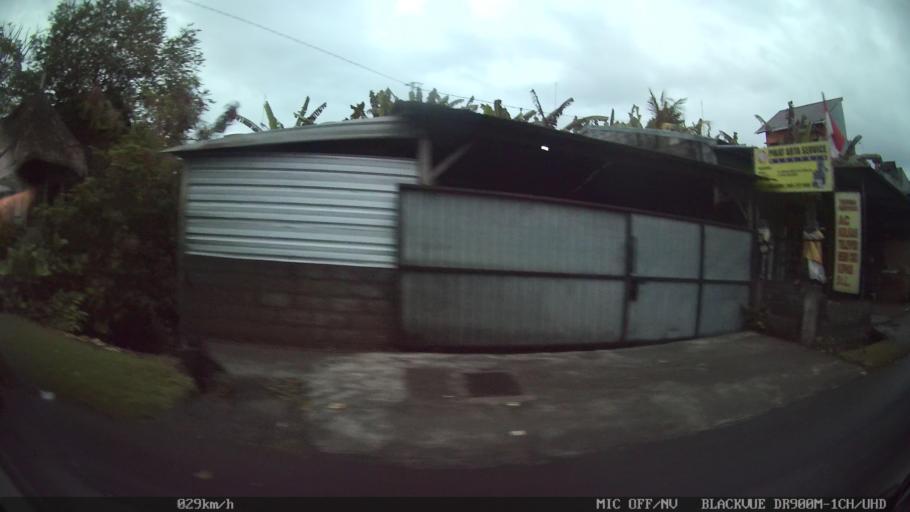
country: ID
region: Bali
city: Banjar Kertajiwa
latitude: -8.6184
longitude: 115.2627
